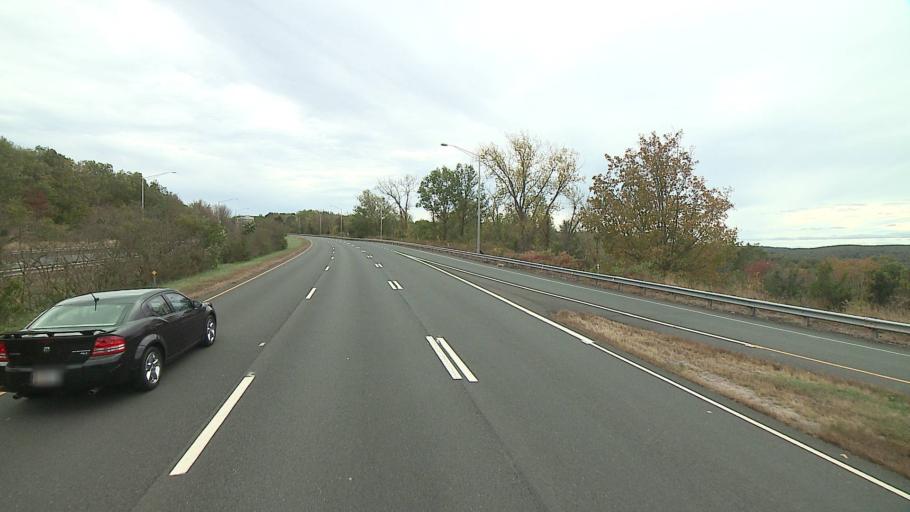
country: US
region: Connecticut
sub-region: Middlesex County
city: Middletown
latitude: 41.5312
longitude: -72.6172
